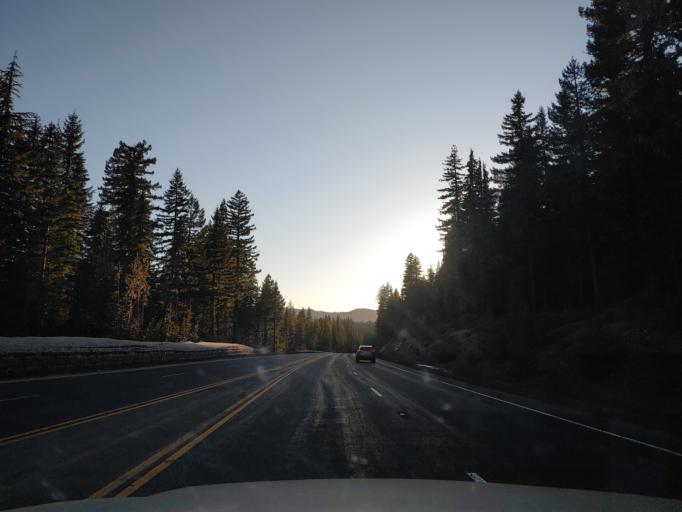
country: US
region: Oregon
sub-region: Lane County
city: Oakridge
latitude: 43.6172
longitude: -122.0859
